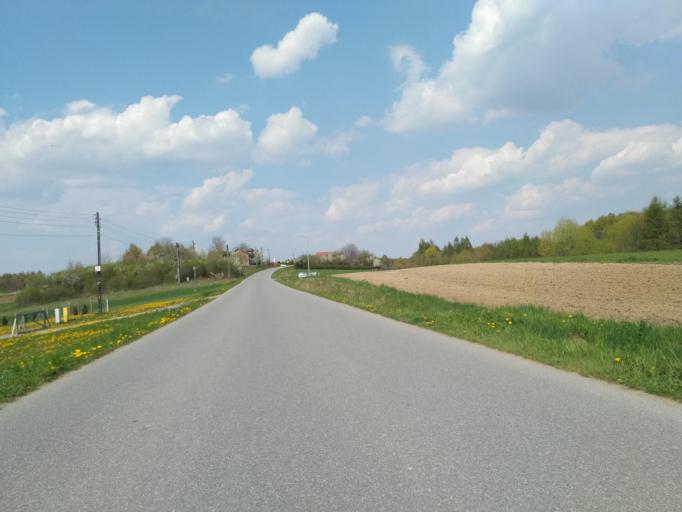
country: PL
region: Subcarpathian Voivodeship
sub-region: Powiat jasielski
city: Debowiec
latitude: 49.6951
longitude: 21.5107
